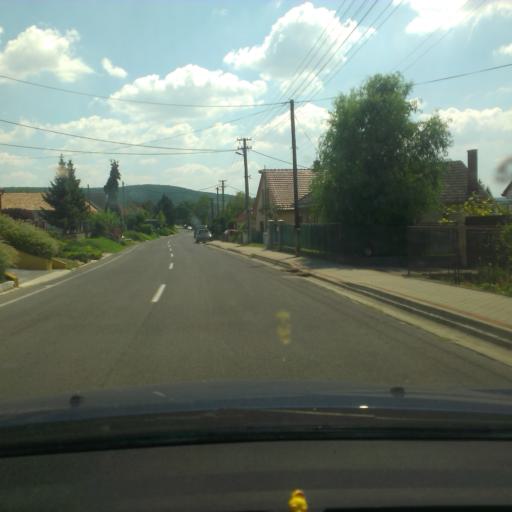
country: SK
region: Trnavsky
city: Hlohovec
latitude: 48.4733
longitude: 17.8086
